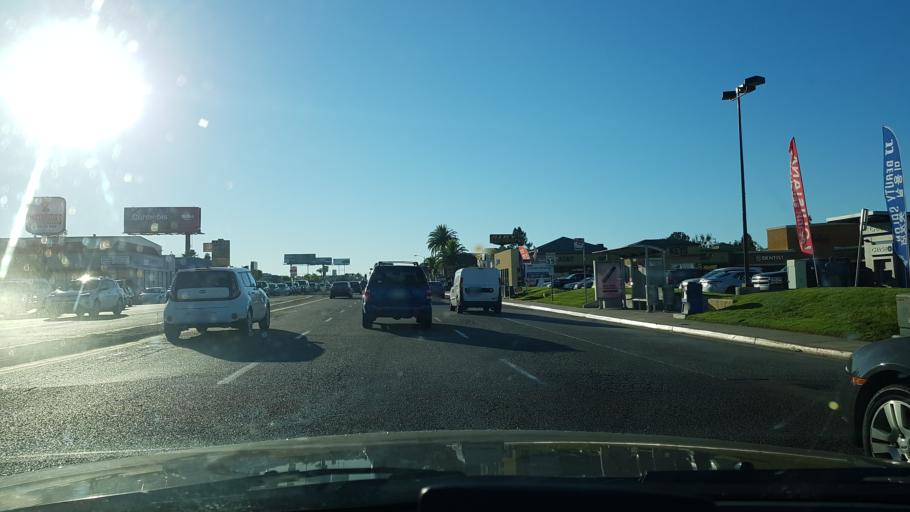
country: US
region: California
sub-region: San Diego County
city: San Diego
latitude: 32.8329
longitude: -117.1489
